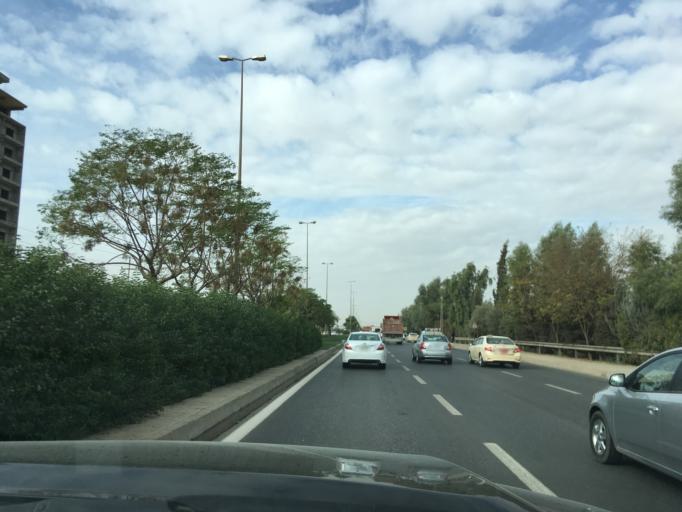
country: IQ
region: Dahuk
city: Dihok
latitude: 36.8471
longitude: 43.0227
